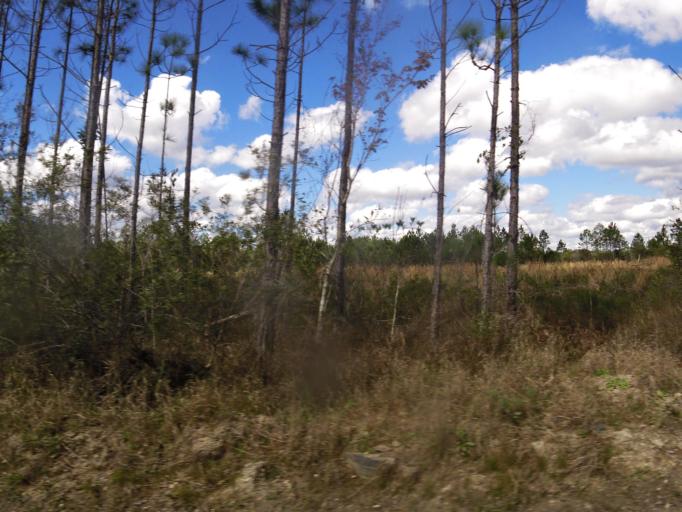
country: US
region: Florida
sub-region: Clay County
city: Green Cove Springs
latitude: 29.8563
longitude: -81.7188
